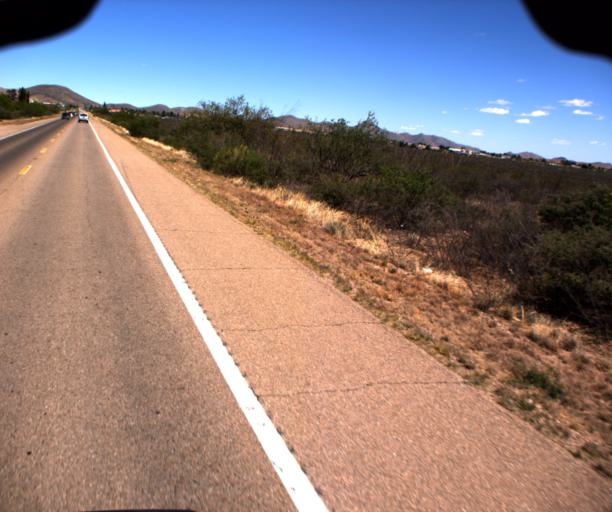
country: US
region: Arizona
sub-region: Cochise County
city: Naco
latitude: 31.3906
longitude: -109.9407
